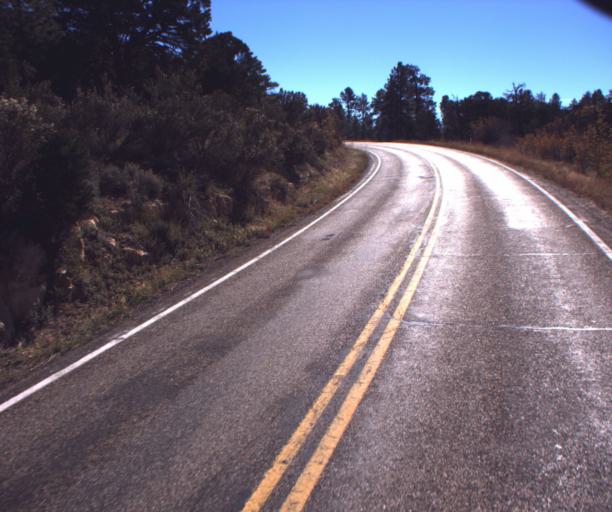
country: US
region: Arizona
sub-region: Coconino County
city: Fredonia
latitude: 36.7756
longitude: -112.2555
